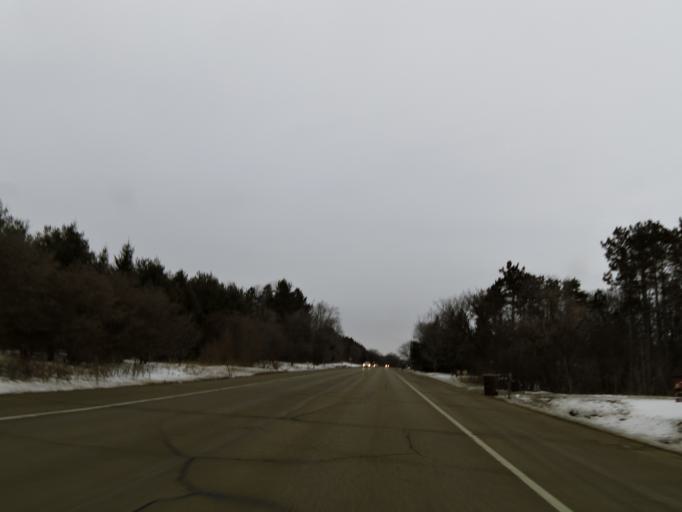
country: US
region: Wisconsin
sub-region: Saint Croix County
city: Hudson
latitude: 44.9766
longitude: -92.7762
